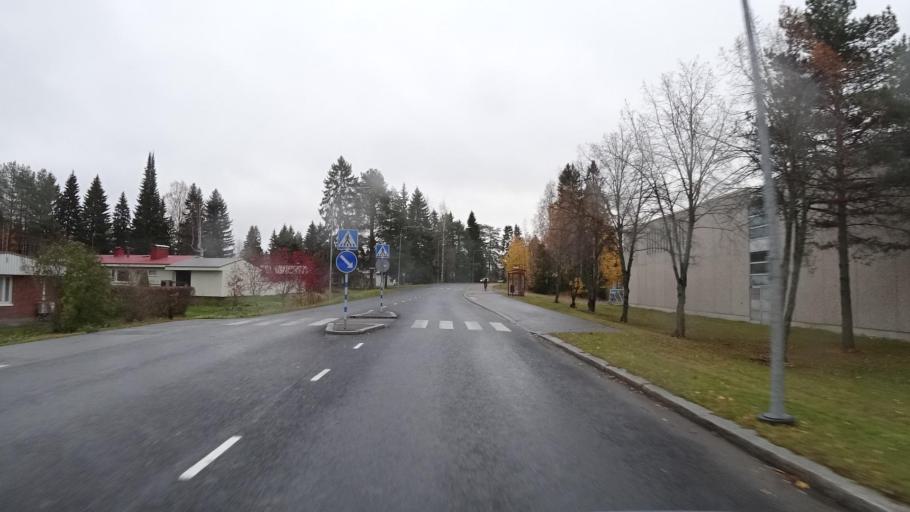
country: FI
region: Northern Savo
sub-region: Kuopio
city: Kuopio
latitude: 62.9300
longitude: 27.6860
